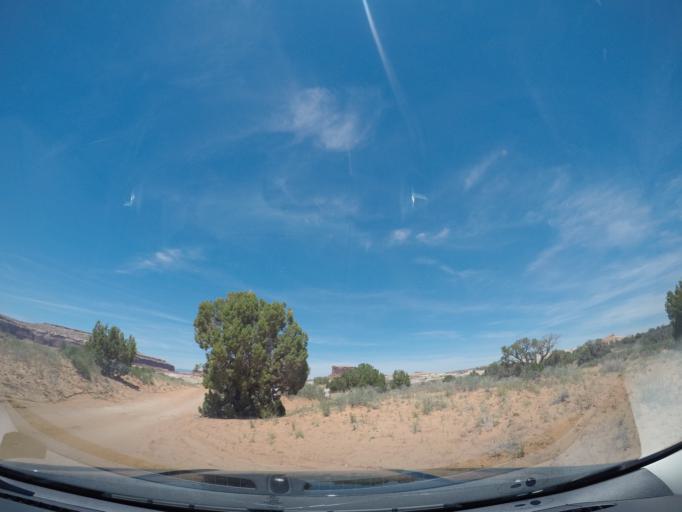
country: US
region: Utah
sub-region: Grand County
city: Moab
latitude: 38.6420
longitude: -109.7473
